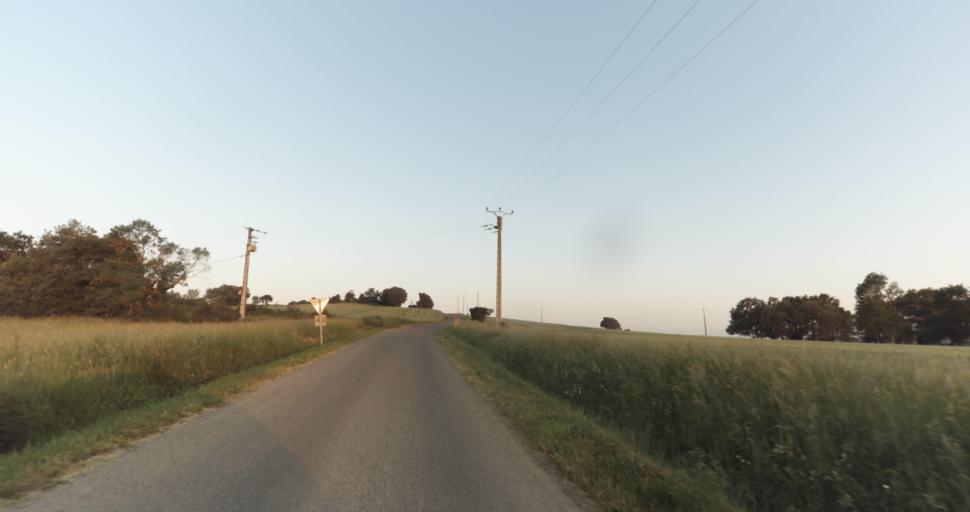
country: FR
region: Midi-Pyrenees
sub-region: Departement du Gers
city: Pujaudran
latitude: 43.6480
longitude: 1.1357
